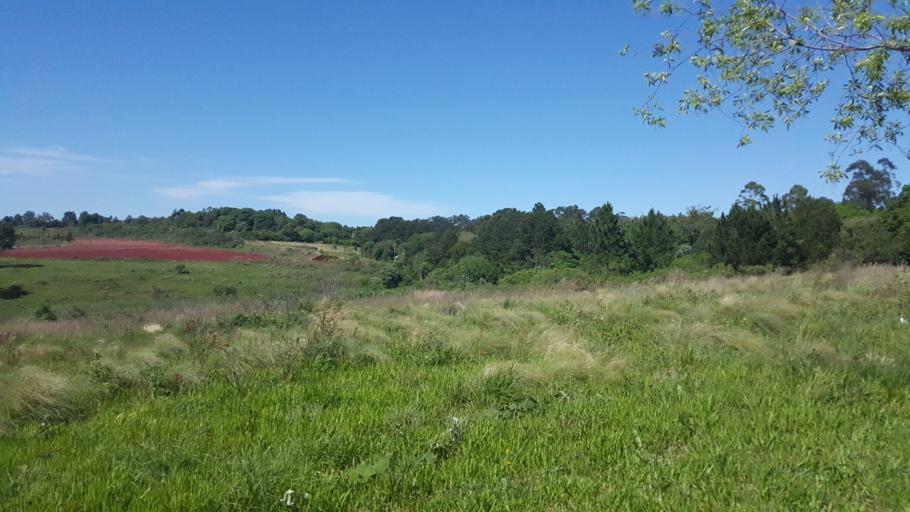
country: AR
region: Misiones
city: Garupa
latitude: -27.4884
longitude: -55.8591
